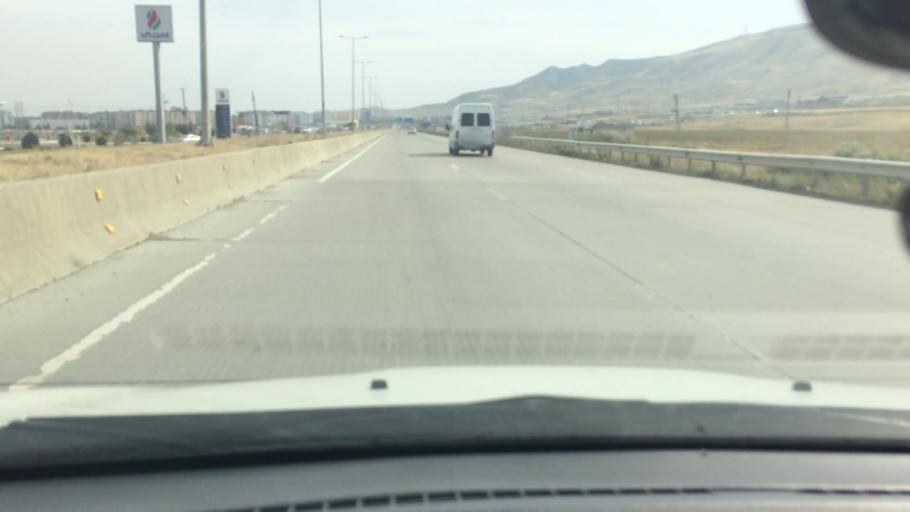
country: GE
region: Kvemo Kartli
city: Rust'avi
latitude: 41.5811
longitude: 44.9531
